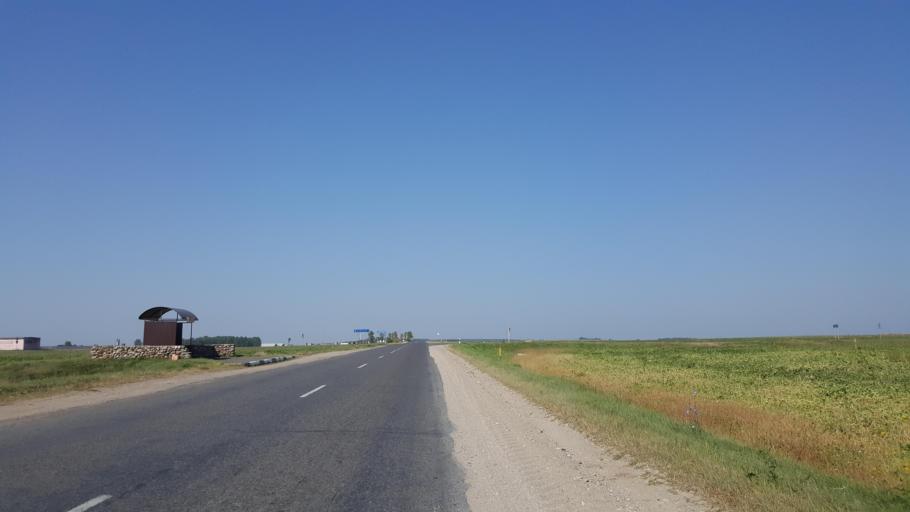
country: BY
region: Brest
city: Kamyanyets
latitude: 52.4145
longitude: 23.6386
